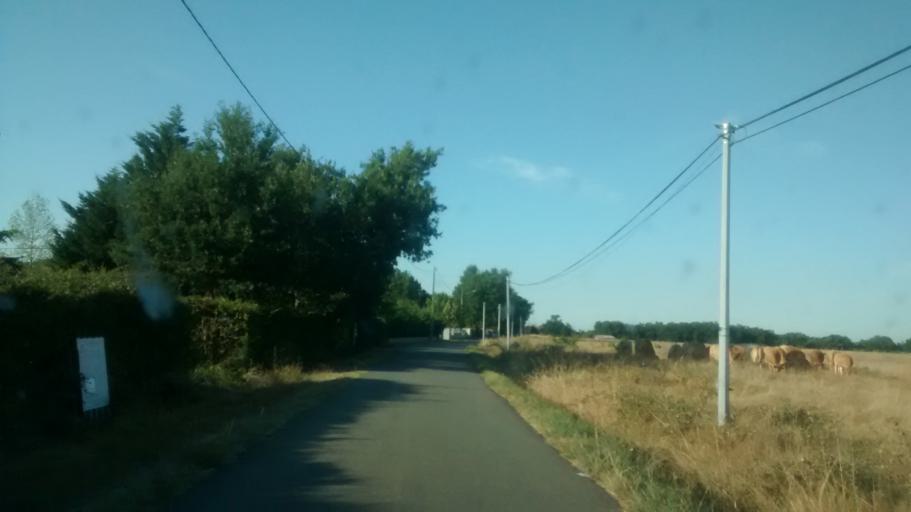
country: FR
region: Midi-Pyrenees
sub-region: Departement de la Haute-Garonne
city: Lherm
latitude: 43.4160
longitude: 1.2158
